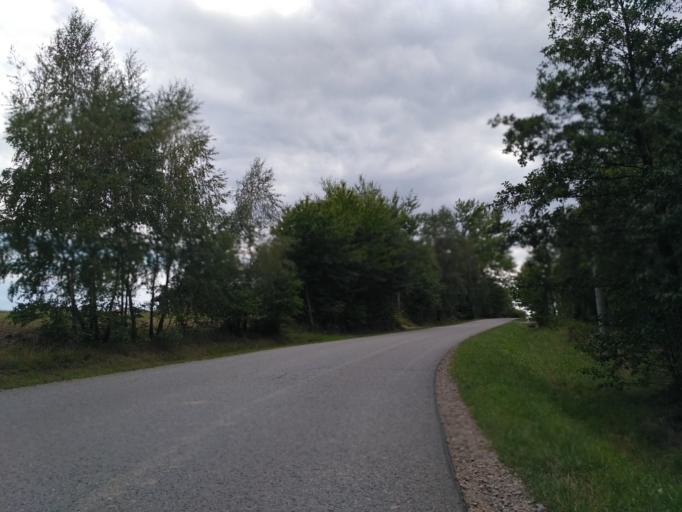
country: PL
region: Subcarpathian Voivodeship
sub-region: Powiat rzeszowski
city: Straszydle
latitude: 49.8834
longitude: 21.9916
